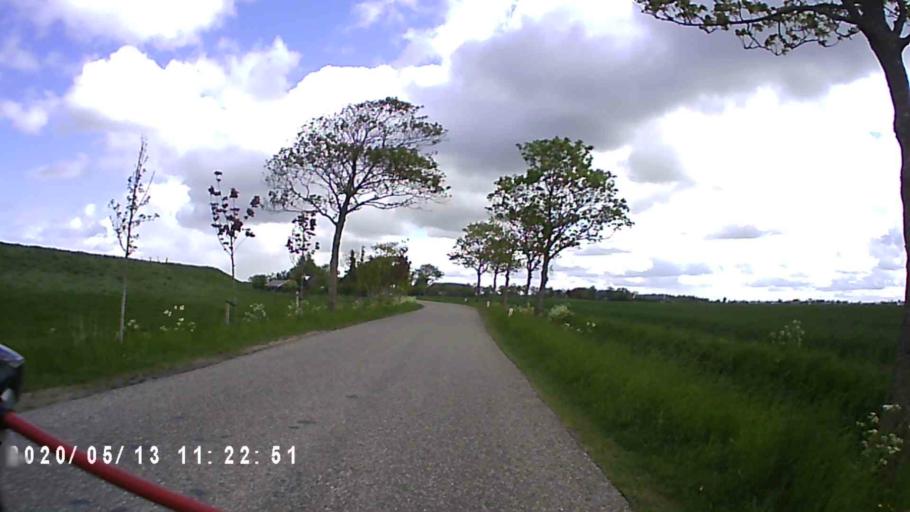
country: NL
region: Groningen
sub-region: Gemeente Zuidhorn
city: Oldehove
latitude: 53.3091
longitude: 6.4000
